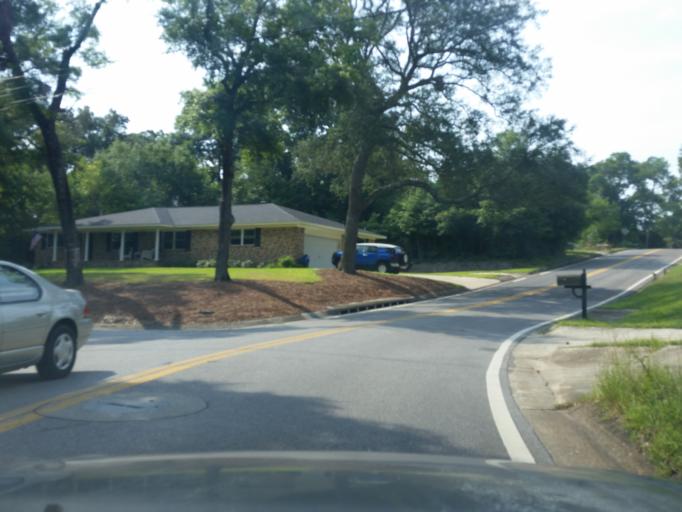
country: US
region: Florida
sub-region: Escambia County
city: Goulding
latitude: 30.4498
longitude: -87.2010
